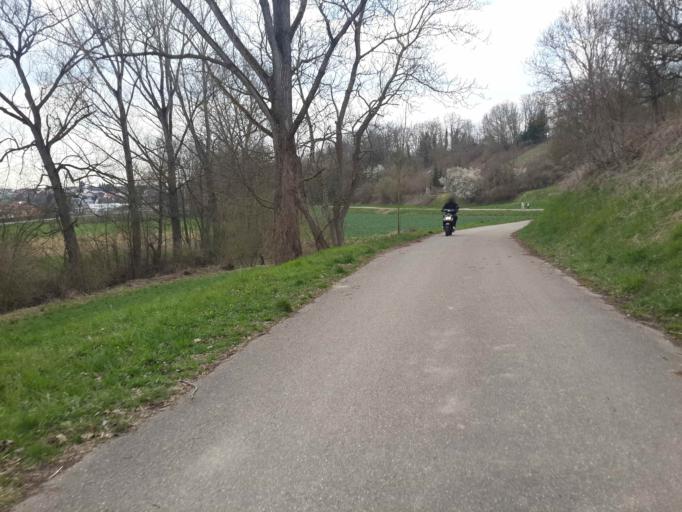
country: DE
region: Baden-Wuerttemberg
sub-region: Karlsruhe Region
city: Balzfeld
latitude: 49.2195
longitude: 8.7941
